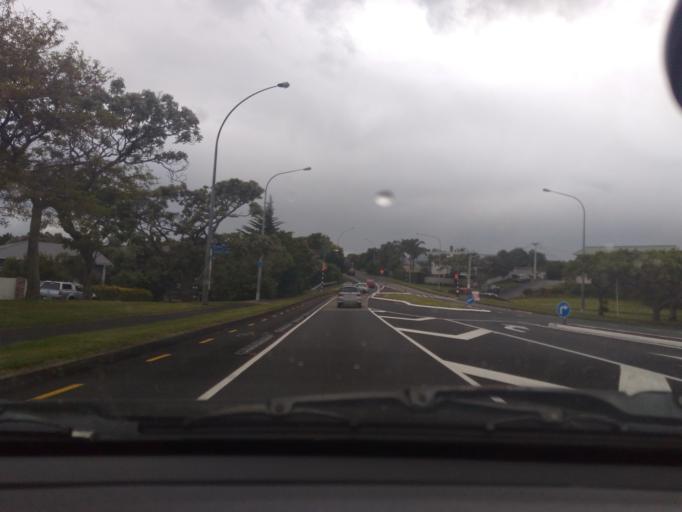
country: NZ
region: Auckland
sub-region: Auckland
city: Auckland
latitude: -36.8747
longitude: 174.7257
